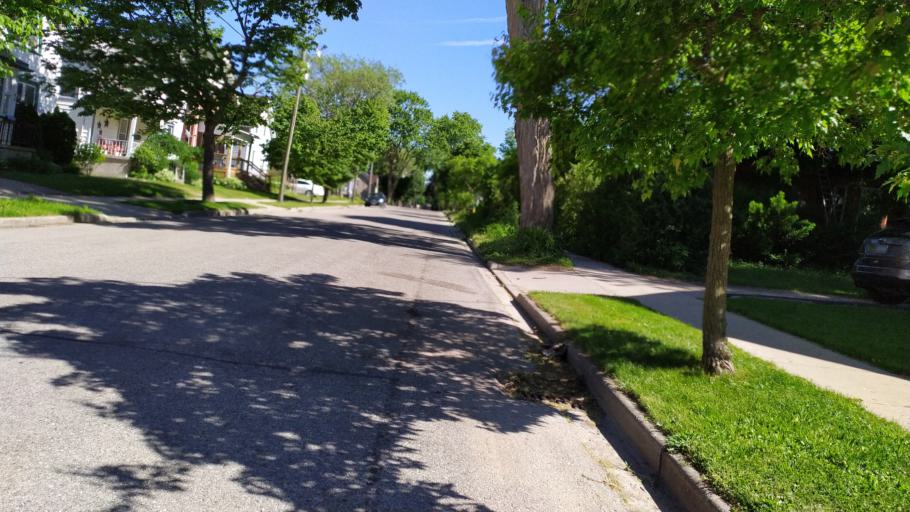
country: CA
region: Ontario
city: Stratford
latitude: 43.3614
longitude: -80.9839
